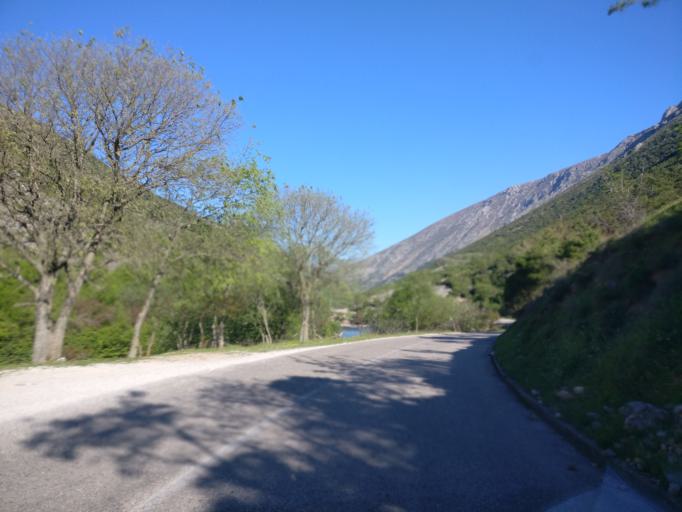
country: BA
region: Federation of Bosnia and Herzegovina
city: Stolac
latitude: 43.0818
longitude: 18.0110
